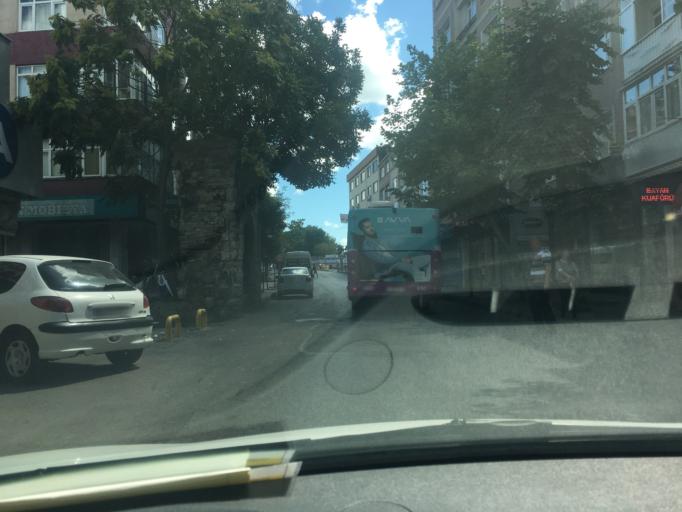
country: TR
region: Istanbul
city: Istanbul
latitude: 41.0048
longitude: 28.9347
